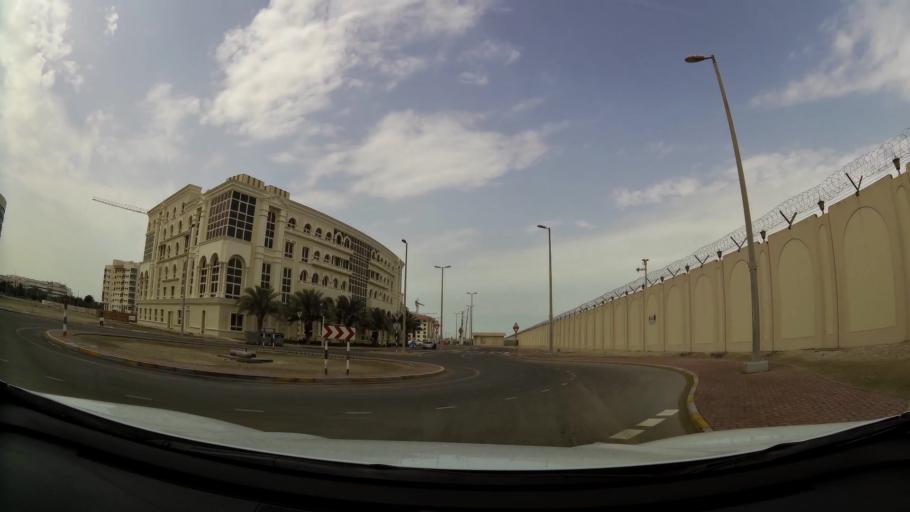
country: AE
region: Abu Dhabi
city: Abu Dhabi
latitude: 24.4191
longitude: 54.4668
